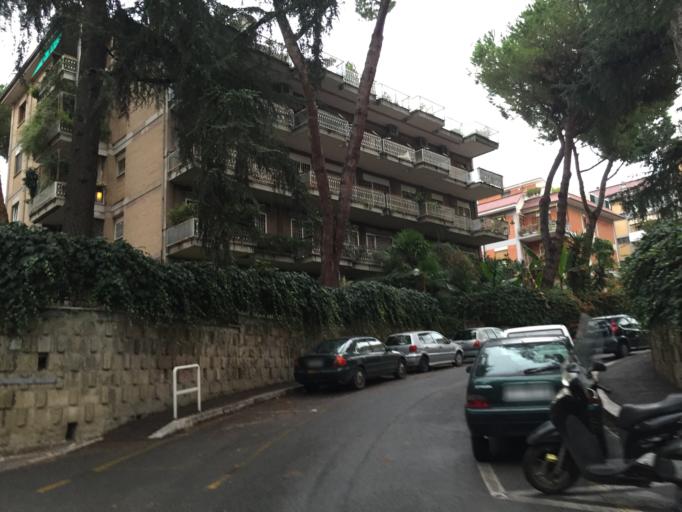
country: VA
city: Vatican City
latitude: 41.8500
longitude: 12.4502
